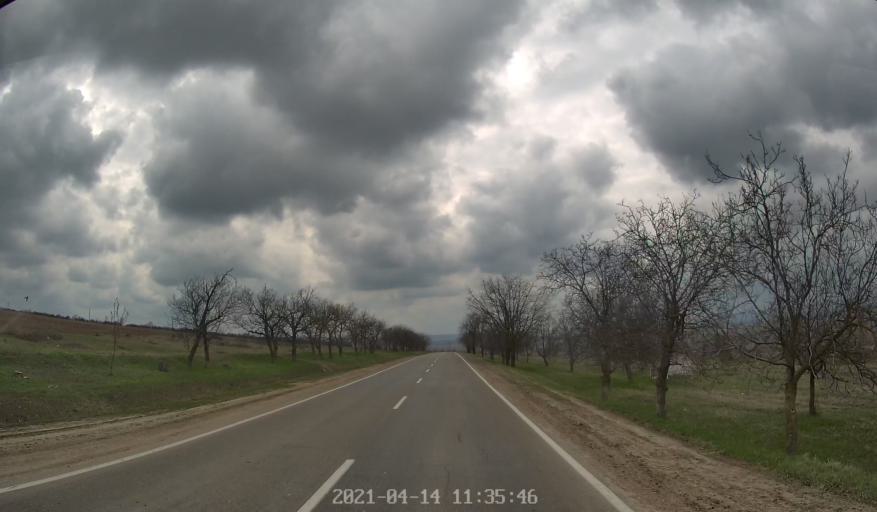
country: MD
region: Criuleni
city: Criuleni
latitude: 47.1663
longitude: 29.1632
